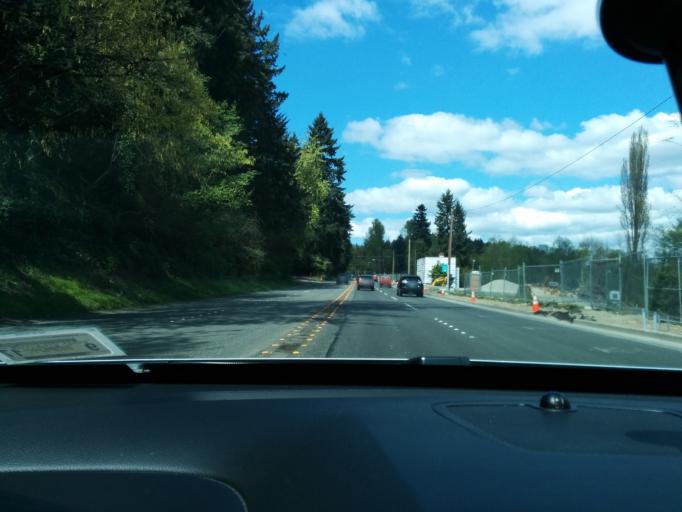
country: US
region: Washington
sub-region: King County
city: Newport
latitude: 47.5898
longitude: -122.1924
